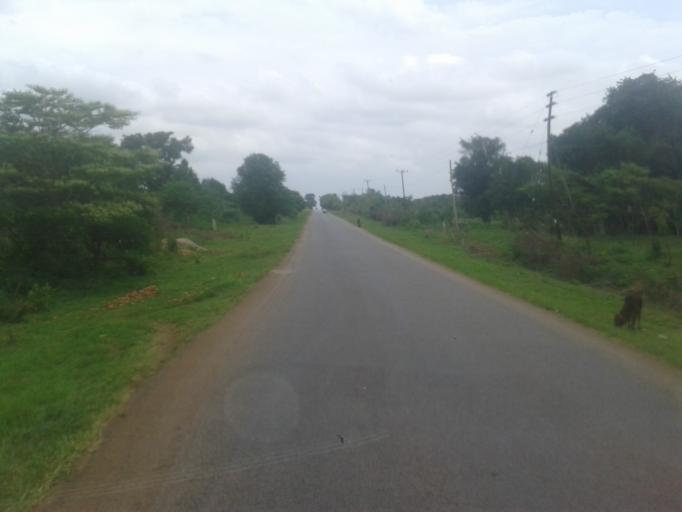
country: UG
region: Western Region
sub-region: Kiryandongo District
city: Masindi Port
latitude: 1.5082
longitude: 32.0952
